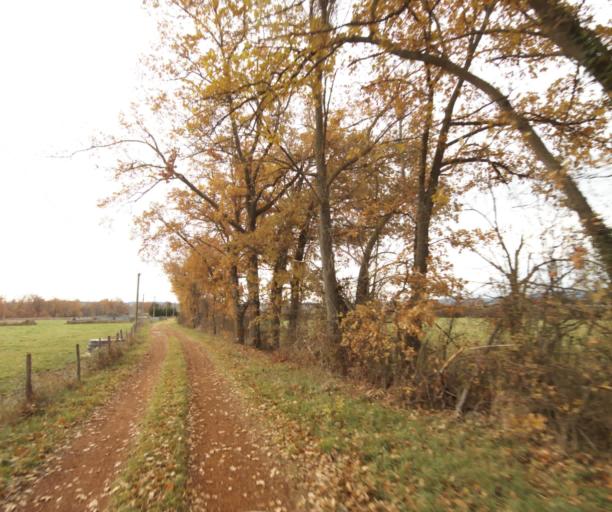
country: FR
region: Rhone-Alpes
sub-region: Departement de la Loire
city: Sury-le-Comtal
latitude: 45.5274
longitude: 4.1998
